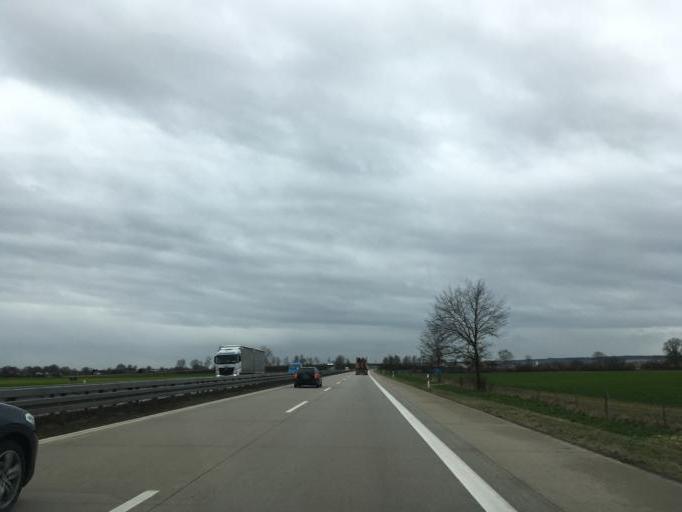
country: DE
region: Bavaria
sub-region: Lower Bavaria
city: Niederaichbach
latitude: 48.6135
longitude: 12.2719
